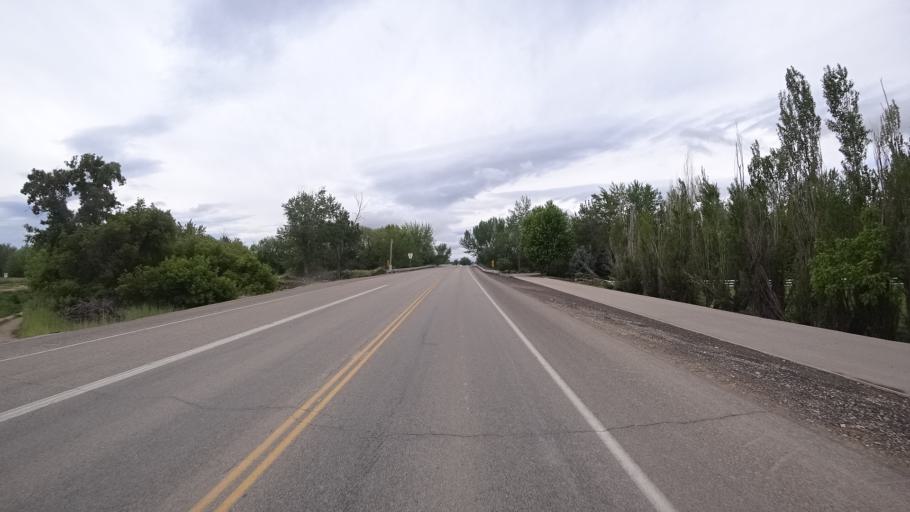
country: US
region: Idaho
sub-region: Ada County
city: Star
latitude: 43.6819
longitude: -116.4932
